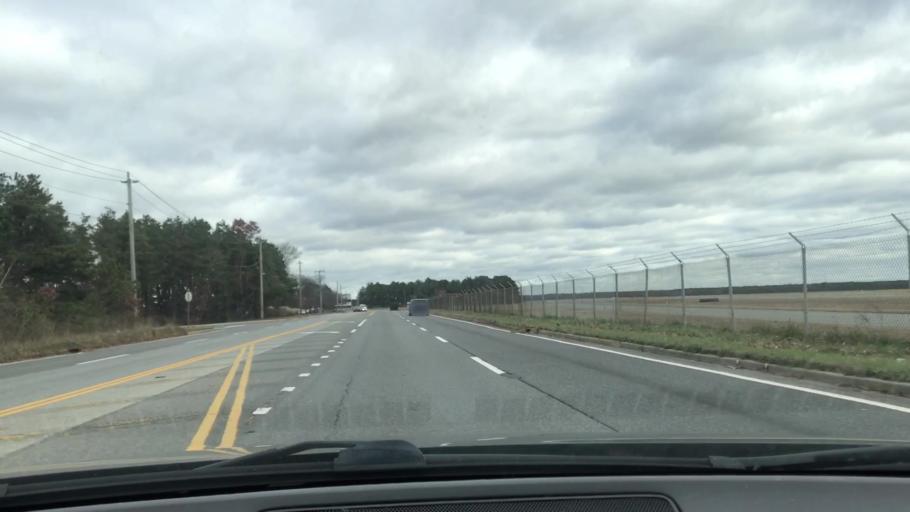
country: US
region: New York
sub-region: Suffolk County
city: Bohemia
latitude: 40.7909
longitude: -73.1138
